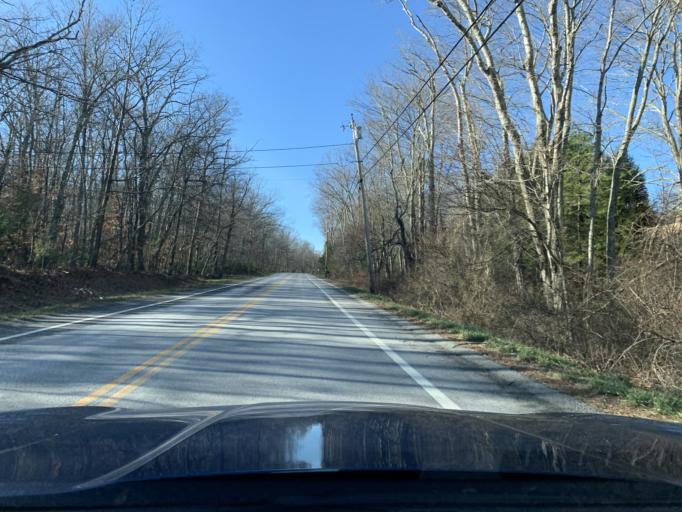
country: US
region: Rhode Island
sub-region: Washington County
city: Hope Valley
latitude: 41.5764
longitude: -71.7594
